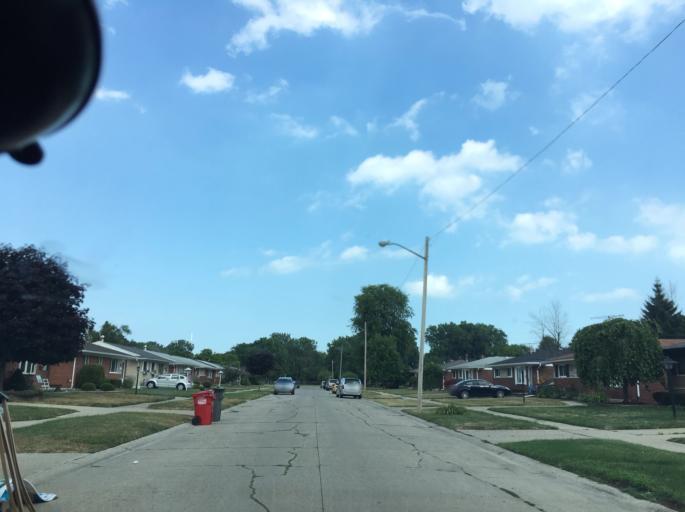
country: US
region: Michigan
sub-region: Macomb County
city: Fraser
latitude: 42.5490
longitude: -82.9131
